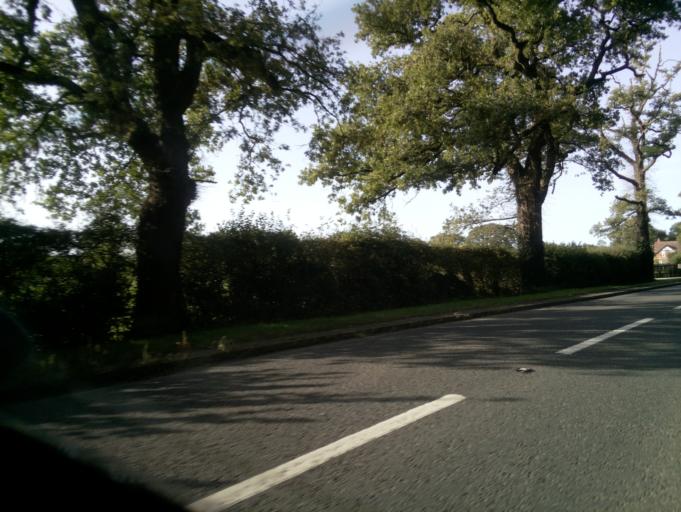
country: GB
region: England
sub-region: Gloucestershire
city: Gloucester
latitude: 51.9131
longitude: -2.2945
